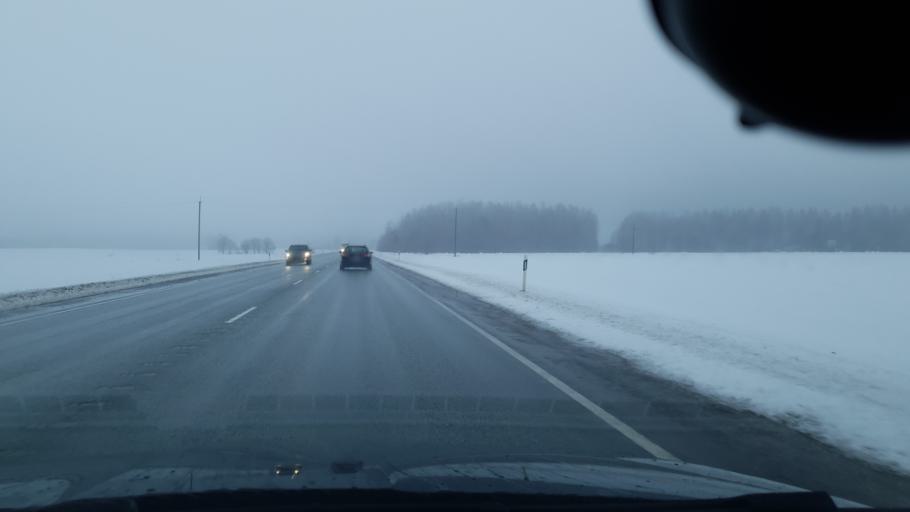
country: EE
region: Jaervamaa
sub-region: Paide linn
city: Paide
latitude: 58.7987
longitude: 25.7581
